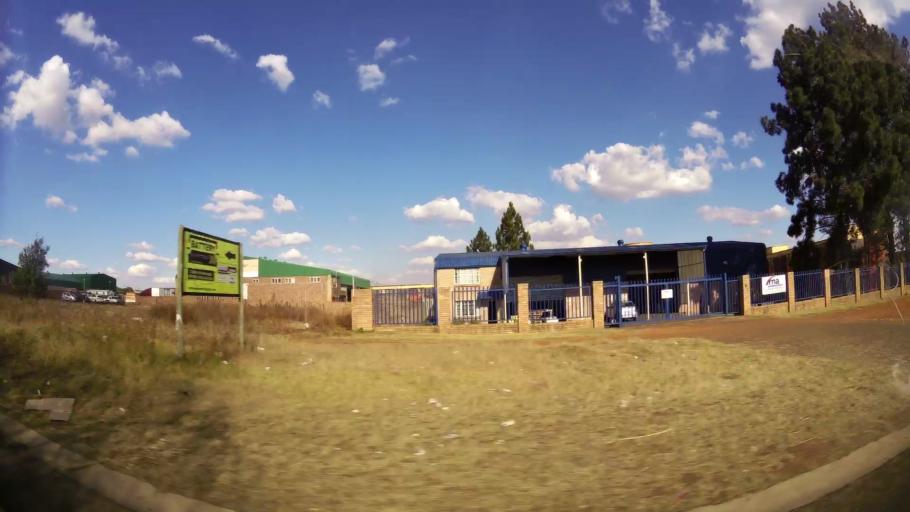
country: ZA
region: Mpumalanga
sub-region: Nkangala District Municipality
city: Witbank
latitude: -25.9009
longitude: 29.2280
